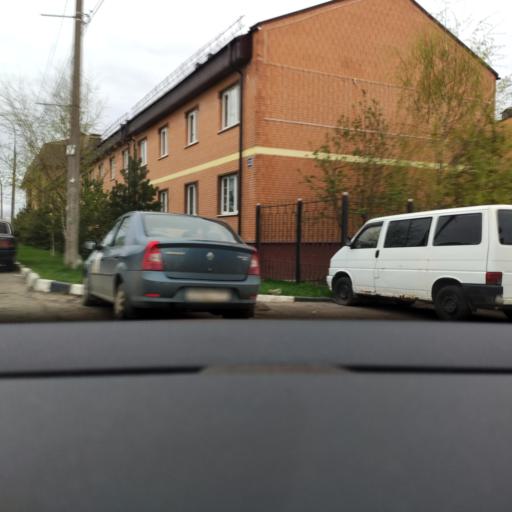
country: RU
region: Moskovskaya
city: Novopodrezkovo
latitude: 55.9924
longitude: 37.3406
